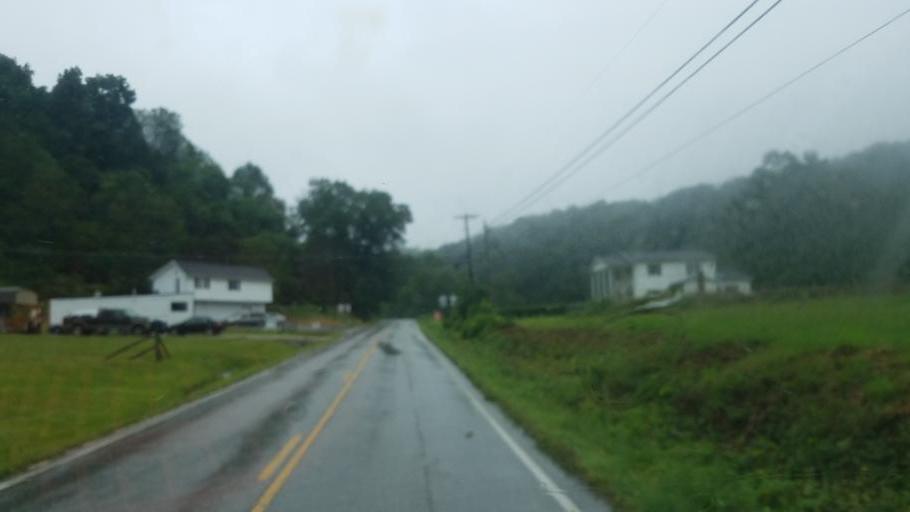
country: US
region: Kentucky
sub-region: Greenup County
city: South Shore
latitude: 38.7078
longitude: -82.9490
